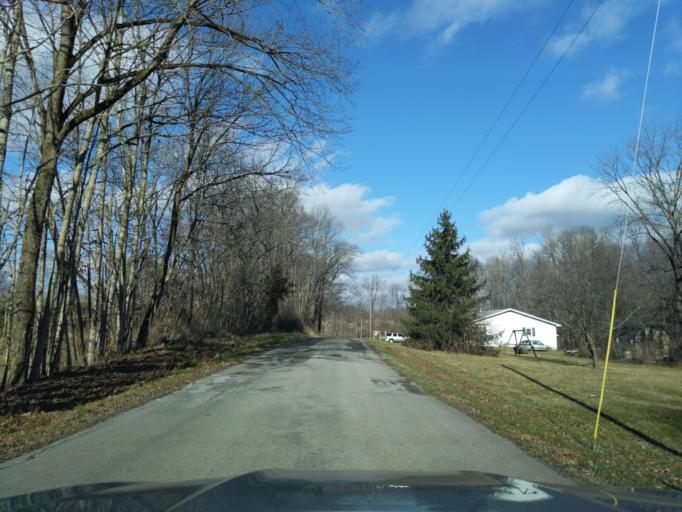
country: US
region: Indiana
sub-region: Decatur County
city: Greensburg
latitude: 39.2747
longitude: -85.4840
